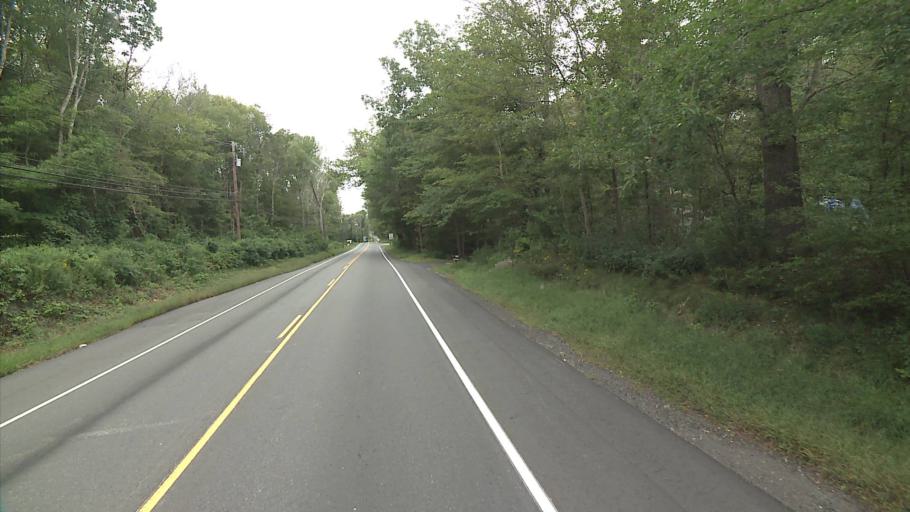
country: US
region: Connecticut
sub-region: New London County
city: Montville Center
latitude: 41.4703
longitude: -72.2580
